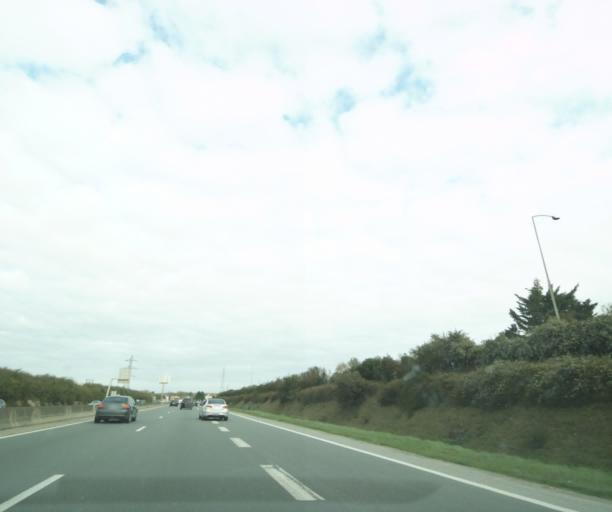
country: FR
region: Poitou-Charentes
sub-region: Departement de la Charente-Maritime
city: Lagord
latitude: 46.1805
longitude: -1.1485
